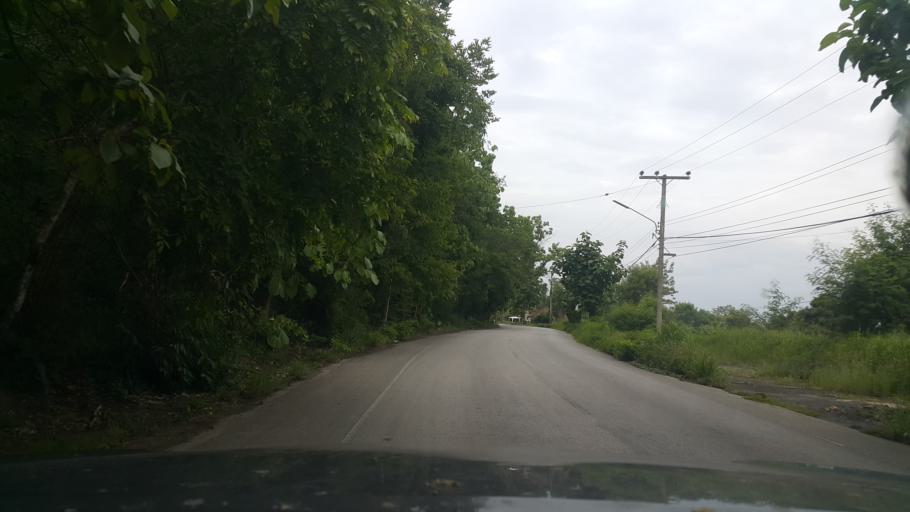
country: TH
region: Chiang Mai
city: San Pa Tong
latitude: 18.6610
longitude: 98.8352
